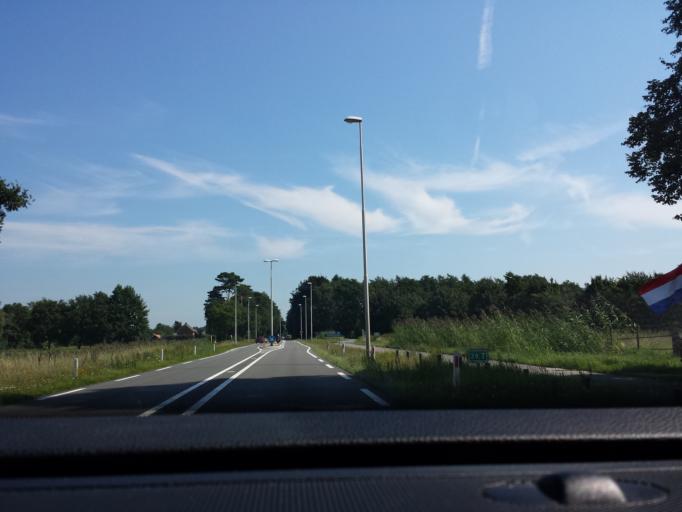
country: NL
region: Overijssel
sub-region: Gemeente Hof van Twente
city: Hengevelde
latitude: 52.2529
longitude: 6.6544
